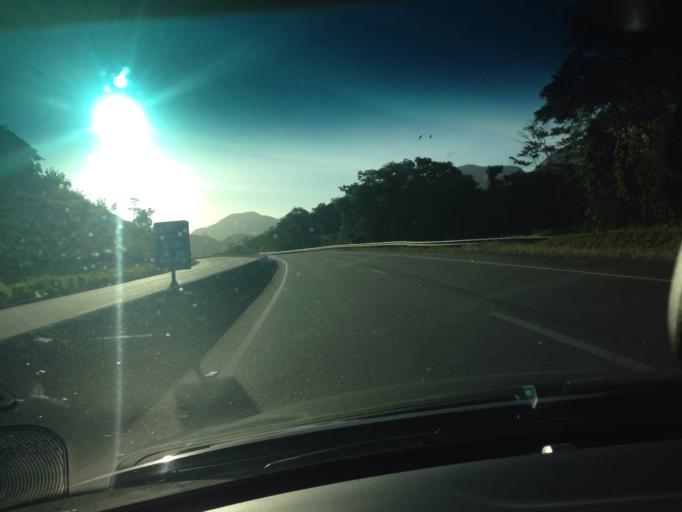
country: BR
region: Espirito Santo
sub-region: Guarapari
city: Guarapari
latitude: -20.6102
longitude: -40.4730
